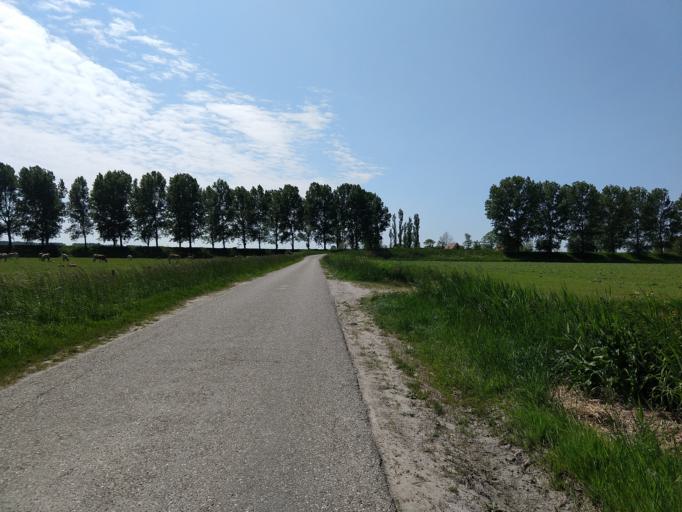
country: NL
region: Zeeland
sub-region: Schouwen-Duiveland
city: Bruinisse
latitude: 51.6018
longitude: 4.0484
